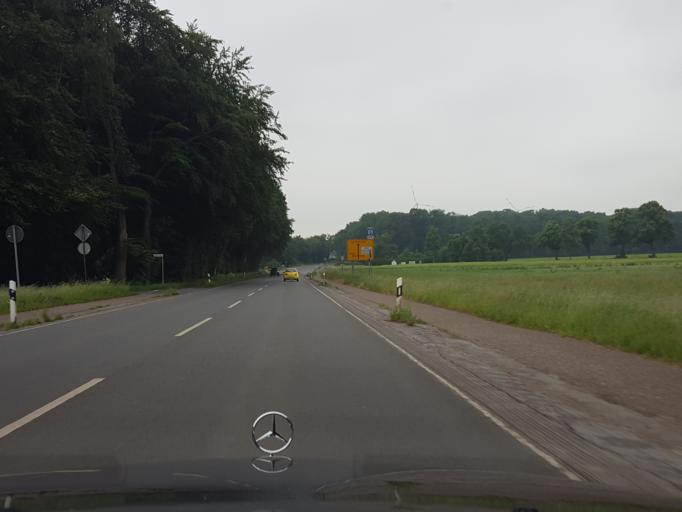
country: DE
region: North Rhine-Westphalia
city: Oer-Erkenschwick
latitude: 51.6774
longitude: 7.2941
